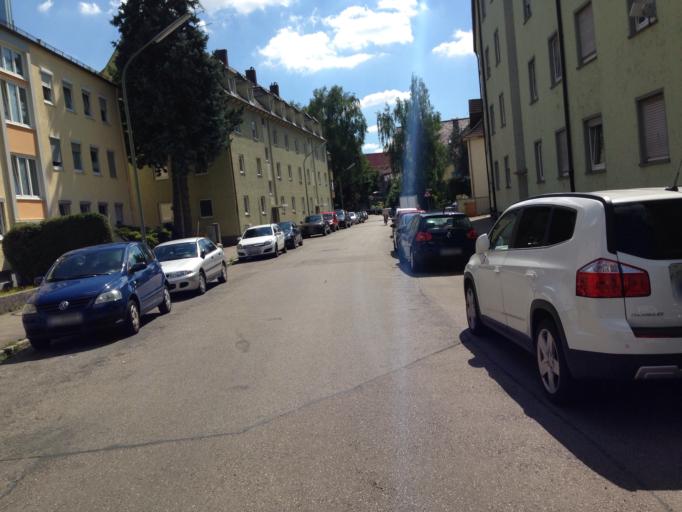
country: DE
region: Bavaria
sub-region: Swabia
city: Stadtbergen
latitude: 48.3604
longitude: 10.8722
